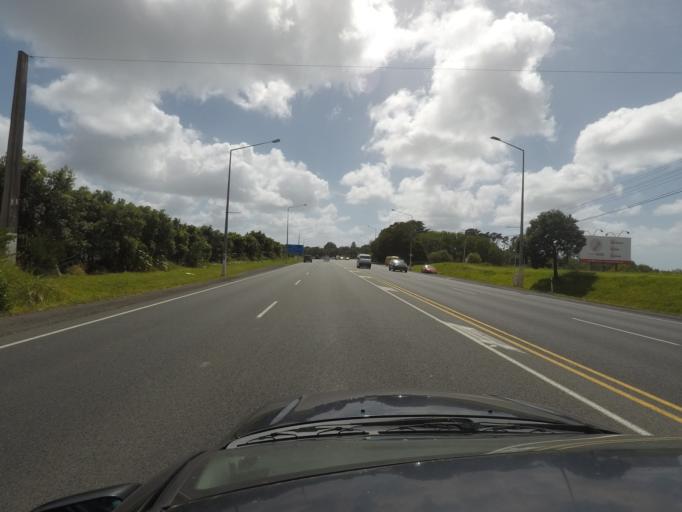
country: NZ
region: Auckland
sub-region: Auckland
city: Rothesay Bay
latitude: -36.6153
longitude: 174.6824
